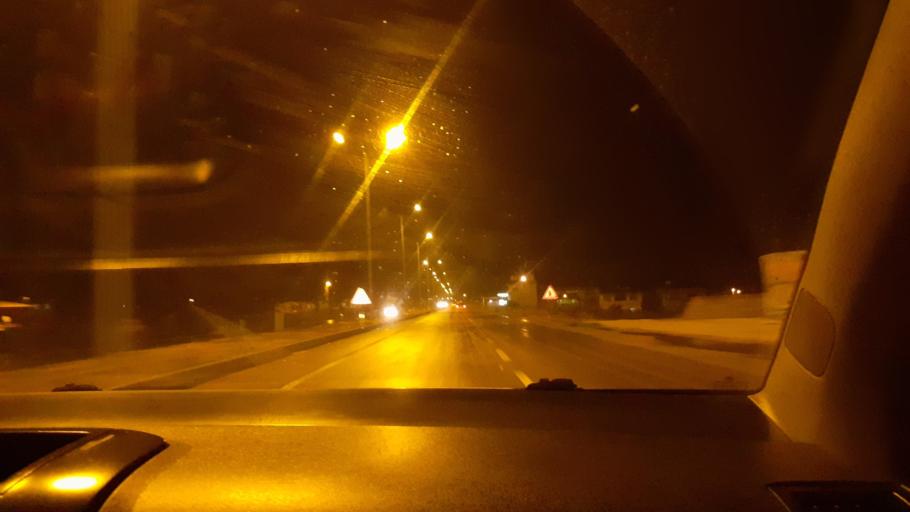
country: TR
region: Hatay
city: Aktepe
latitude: 36.7069
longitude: 36.4887
